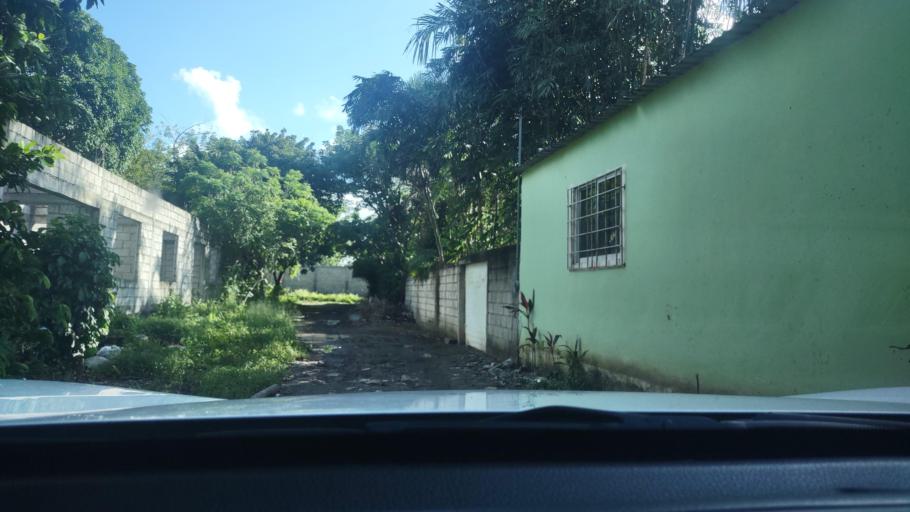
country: MX
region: Veracruz
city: El Tejar
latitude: 19.0717
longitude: -96.1568
